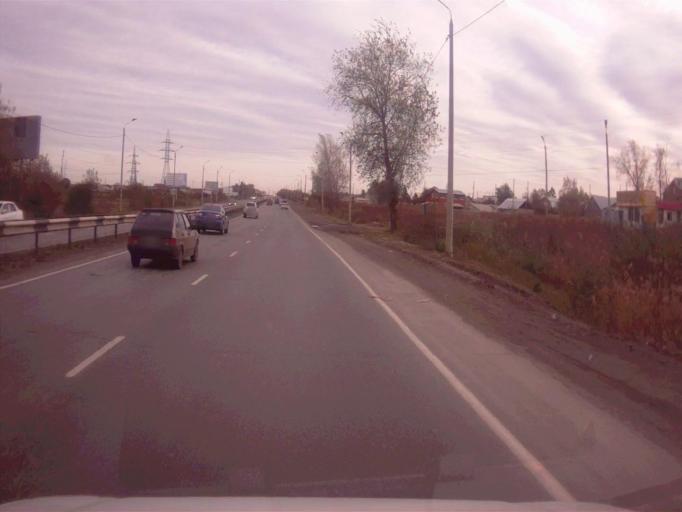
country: RU
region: Chelyabinsk
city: Novosineglazovskiy
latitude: 55.0464
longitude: 61.4180
